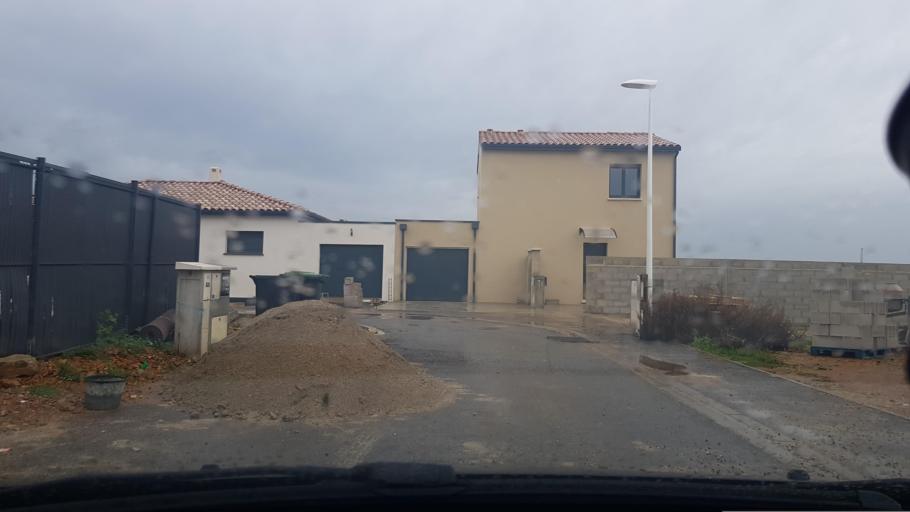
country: FR
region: Languedoc-Roussillon
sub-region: Departement du Gard
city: Bellegarde
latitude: 43.7555
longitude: 4.4962
